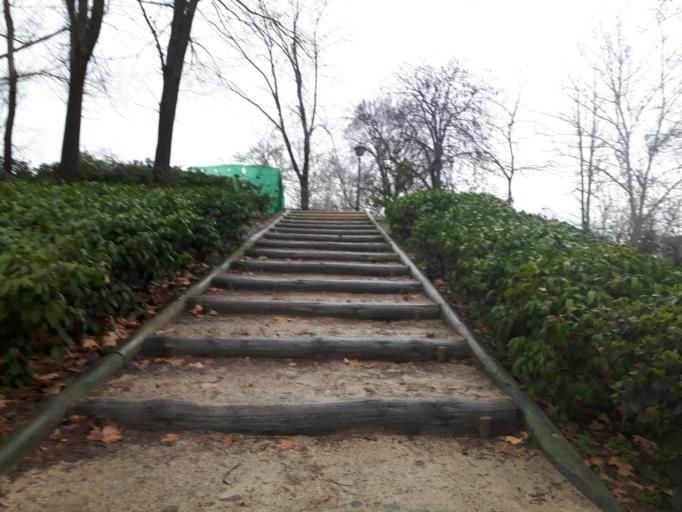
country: ES
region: Madrid
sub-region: Provincia de Madrid
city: Moncloa-Aravaca
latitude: 40.4197
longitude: -3.7293
